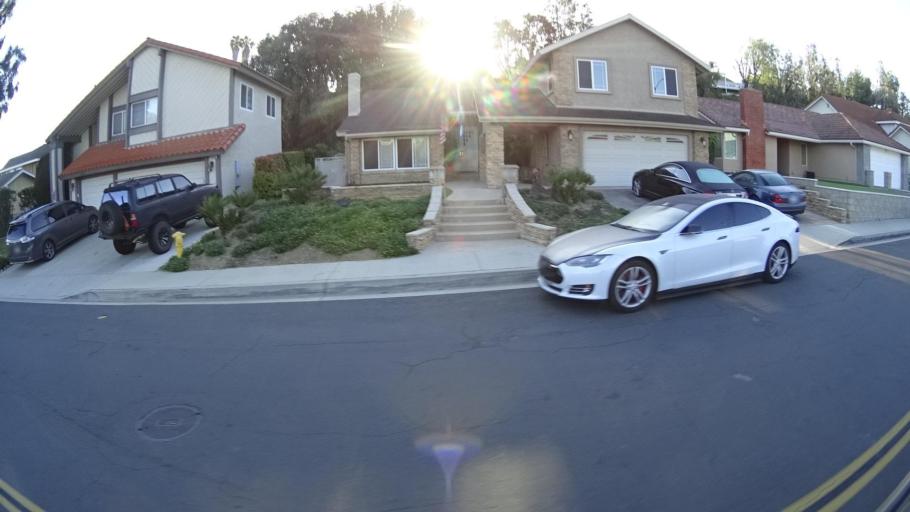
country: US
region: California
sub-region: Los Angeles County
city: Walnut
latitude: 33.9678
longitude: -117.8406
